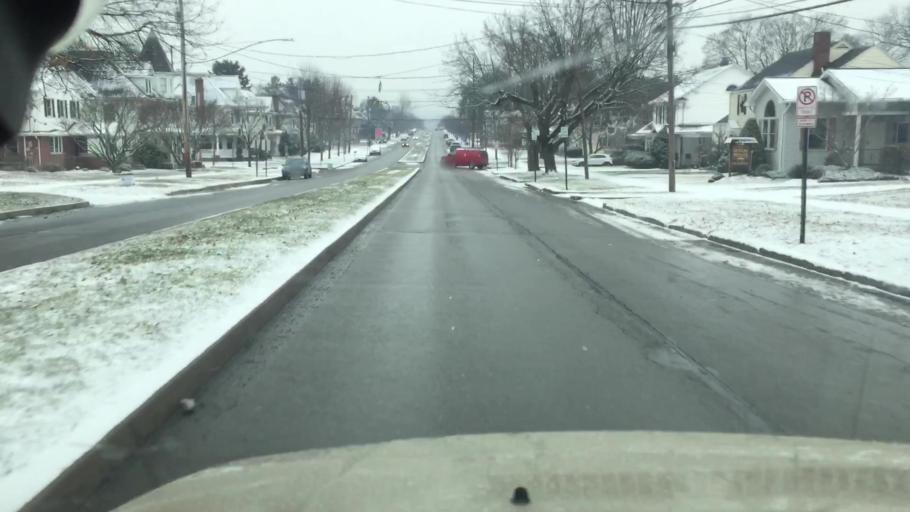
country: US
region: Pennsylvania
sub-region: Columbia County
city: Berwick
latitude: 41.0620
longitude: -76.2398
